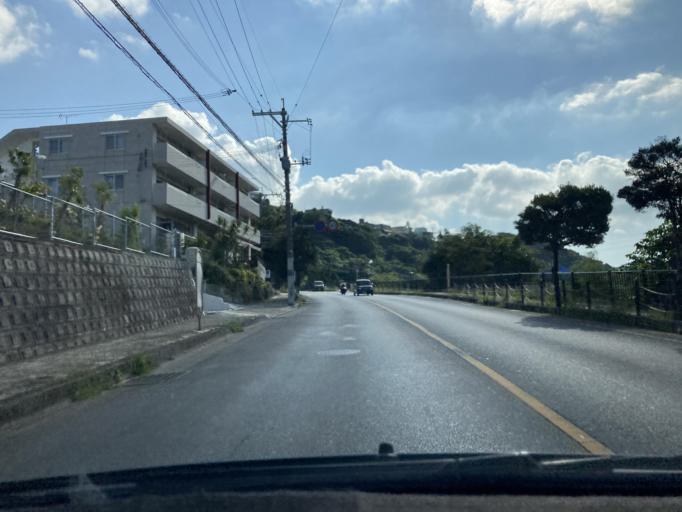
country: JP
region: Okinawa
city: Naha-shi
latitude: 26.2131
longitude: 127.7174
